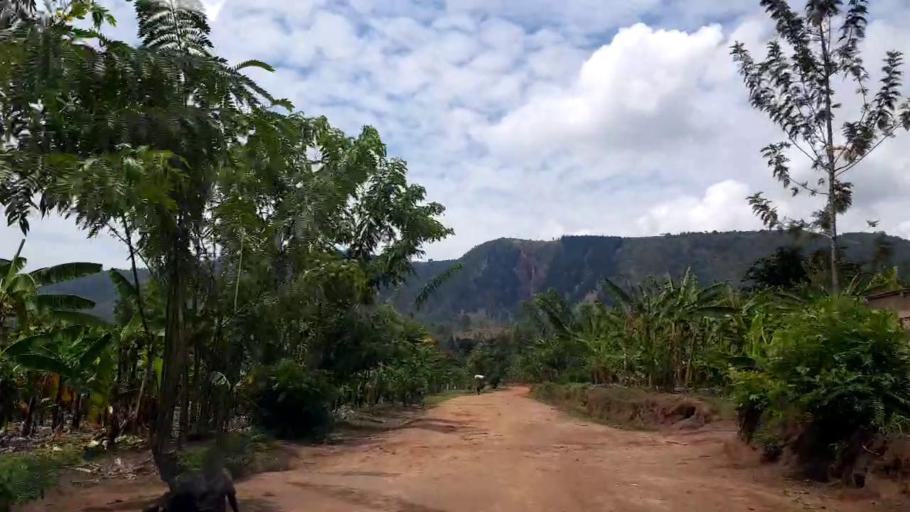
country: RW
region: Northern Province
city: Byumba
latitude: -1.4915
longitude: 30.1976
